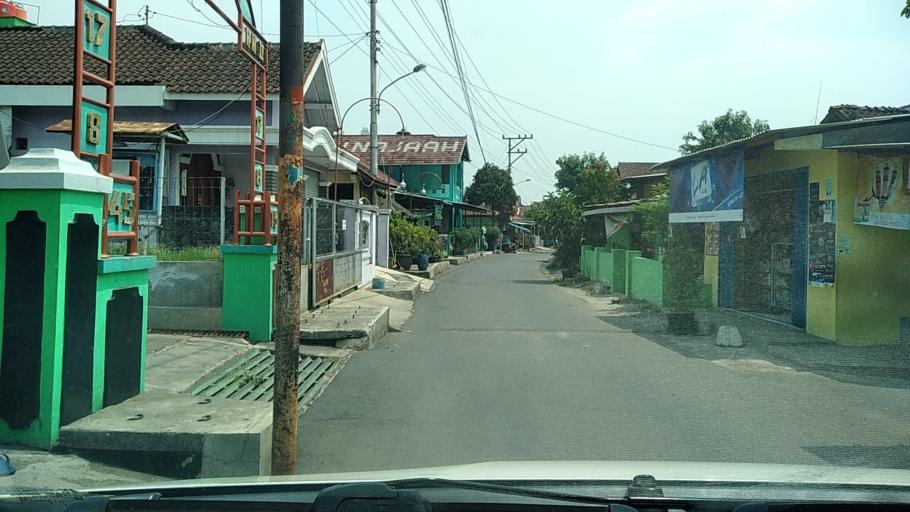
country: ID
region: Central Java
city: Semarang
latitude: -6.9859
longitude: 110.3625
